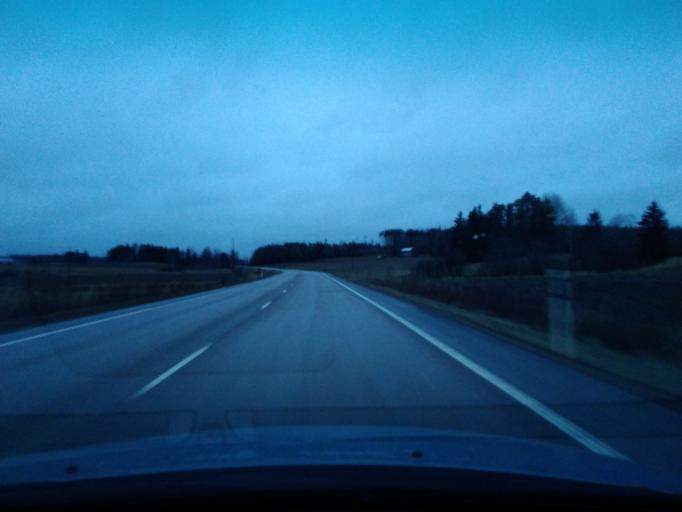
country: FI
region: Uusimaa
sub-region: Porvoo
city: Askola
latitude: 60.4623
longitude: 25.5779
